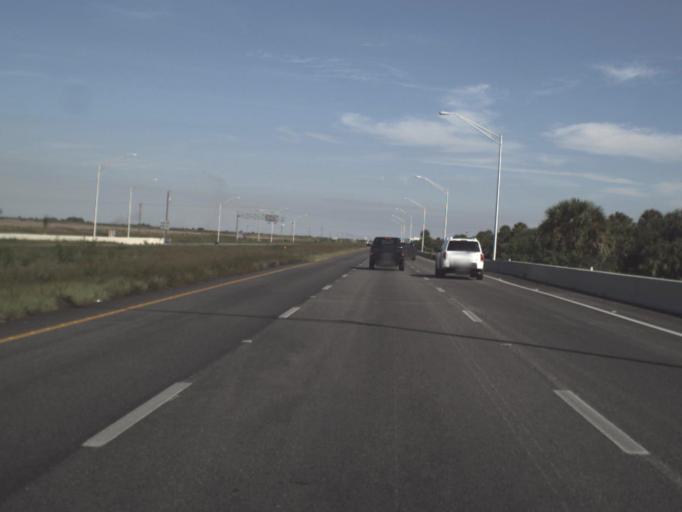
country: US
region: Florida
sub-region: Glades County
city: Moore Haven
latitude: 26.7534
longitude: -81.0774
